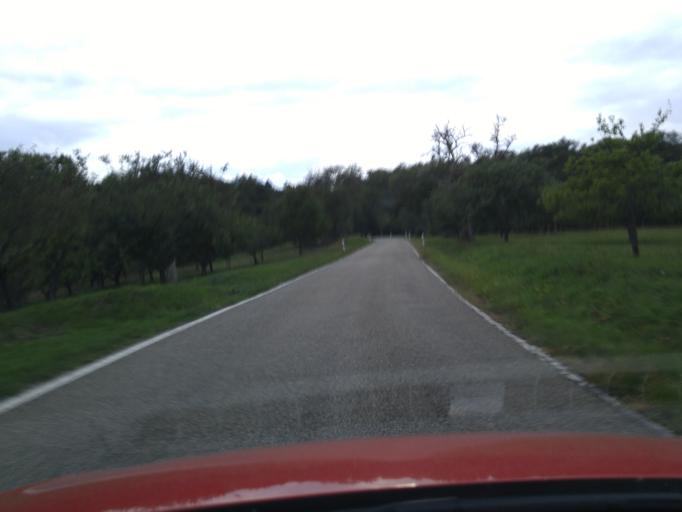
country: DE
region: Baden-Wuerttemberg
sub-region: Regierungsbezirk Stuttgart
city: Zaberfeld
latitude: 49.0459
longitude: 8.9233
